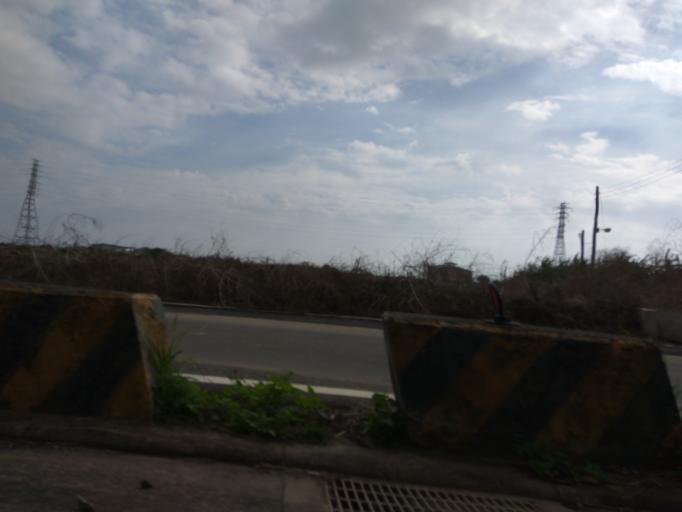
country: TW
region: Taiwan
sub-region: Hsinchu
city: Zhubei
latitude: 24.9741
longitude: 121.0179
